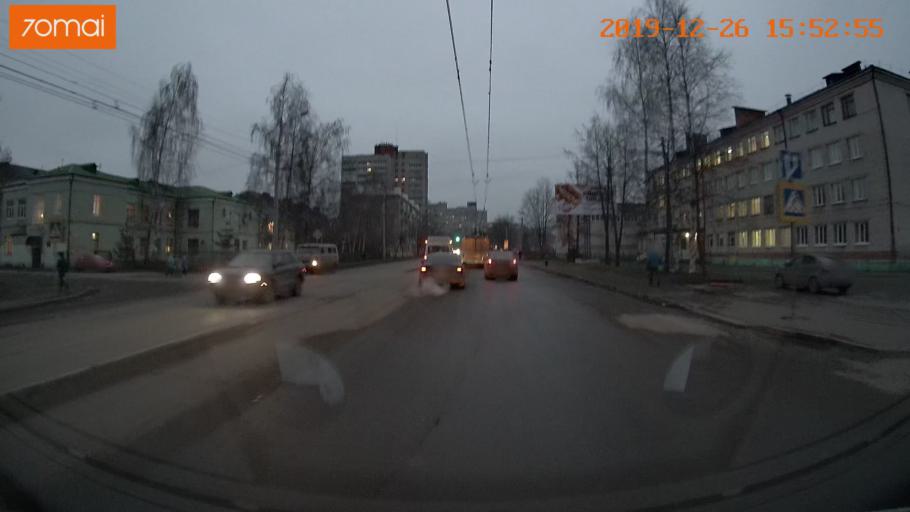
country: RU
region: Jaroslavl
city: Rybinsk
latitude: 58.0499
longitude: 38.8239
